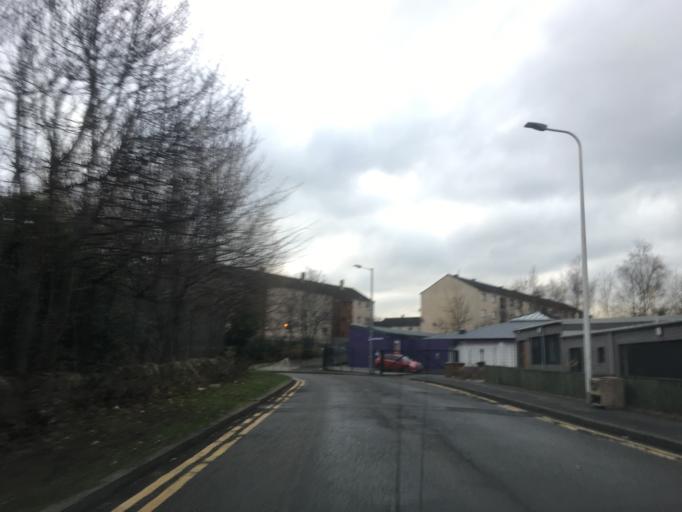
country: GB
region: Scotland
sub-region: Edinburgh
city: Colinton
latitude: 55.9196
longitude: -3.2731
